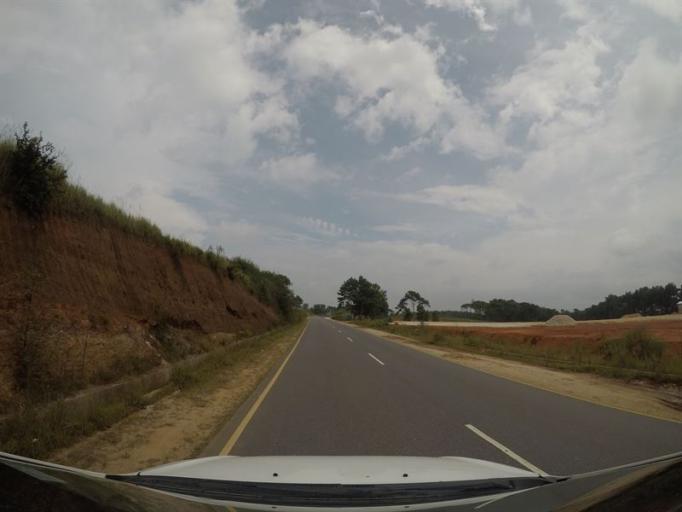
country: IN
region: Meghalaya
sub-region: East Khasi Hills
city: Shillong
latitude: 25.4907
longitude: 92.1861
